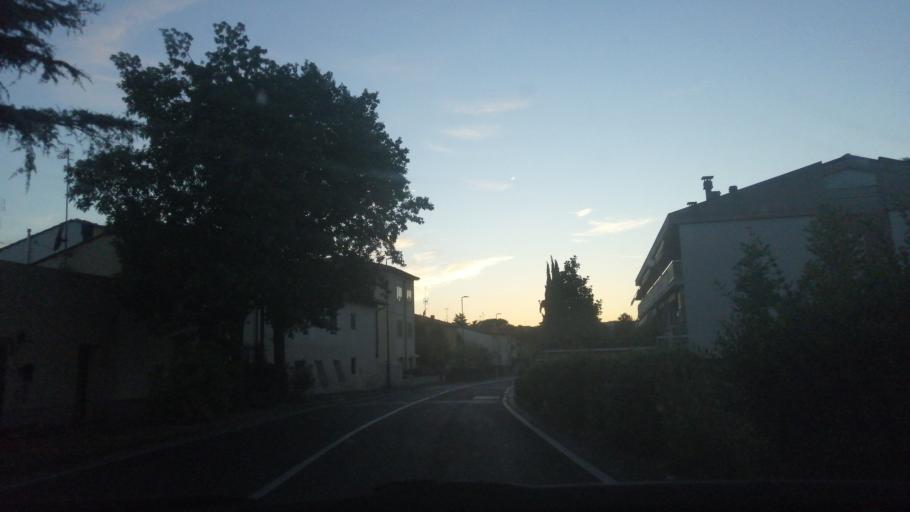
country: IT
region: Tuscany
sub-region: Province of Florence
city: Sesto Fiorentino
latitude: 43.8392
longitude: 11.2029
